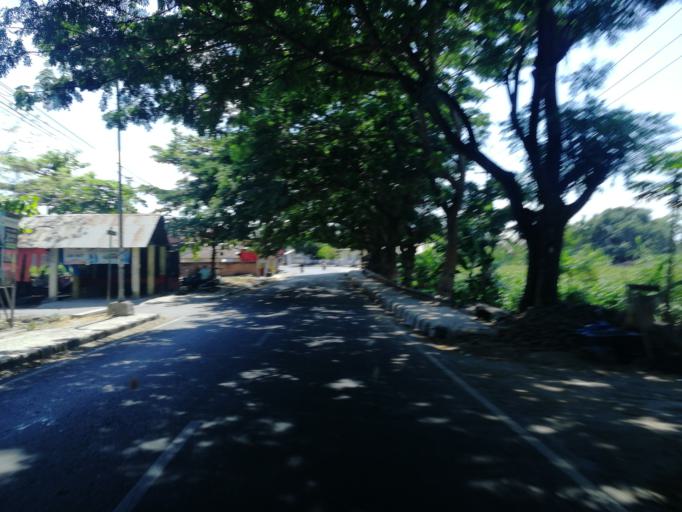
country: ID
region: West Nusa Tenggara
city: Kediri
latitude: -8.6885
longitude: 116.1190
